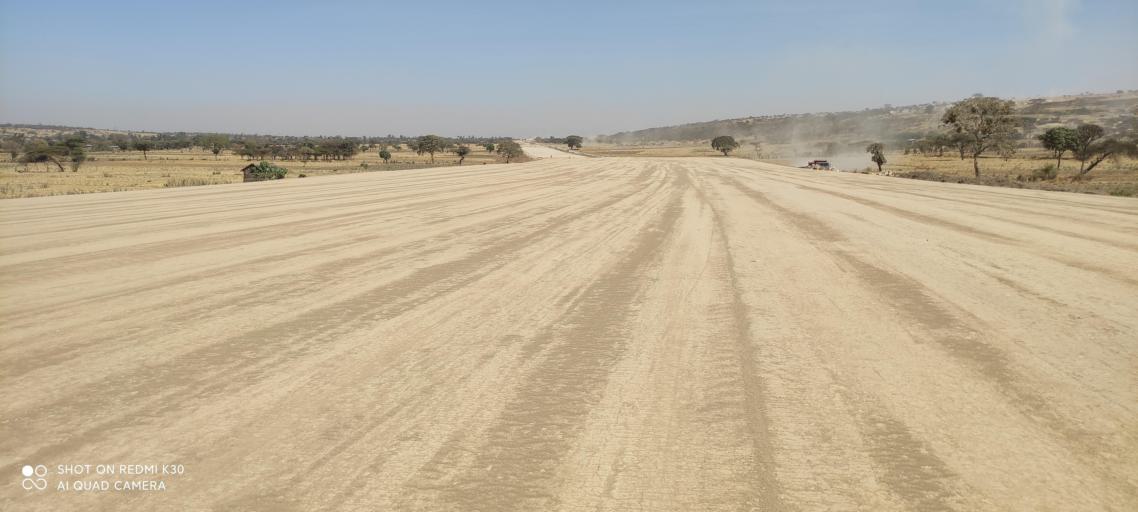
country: ET
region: Oromiya
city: Shashemene
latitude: 7.3953
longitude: 38.6583
